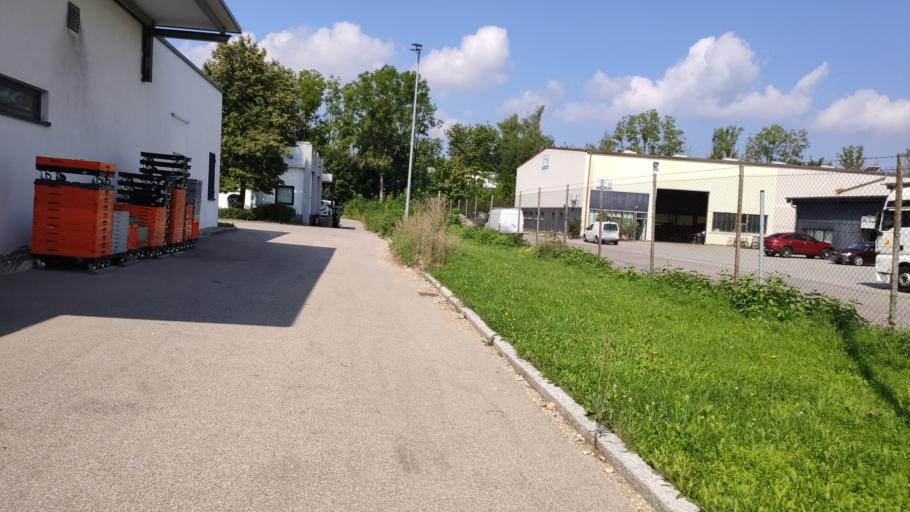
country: DE
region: Bavaria
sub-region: Swabia
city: Bobingen
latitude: 48.2656
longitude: 10.8394
